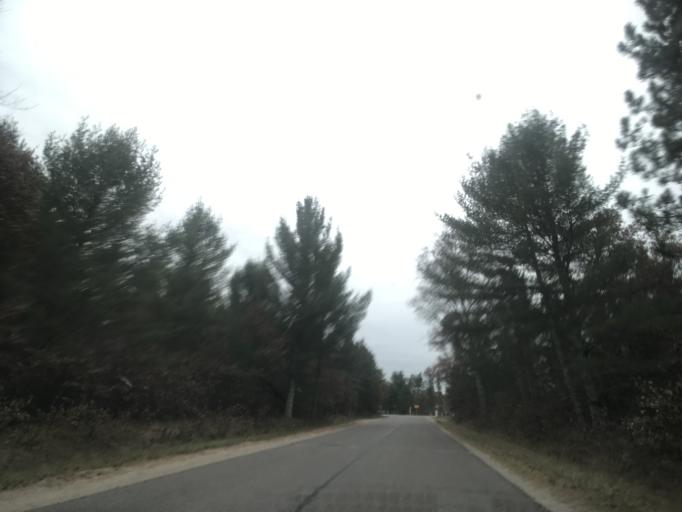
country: US
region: Wisconsin
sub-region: Oconto County
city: Gillett
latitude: 45.2517
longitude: -88.2521
